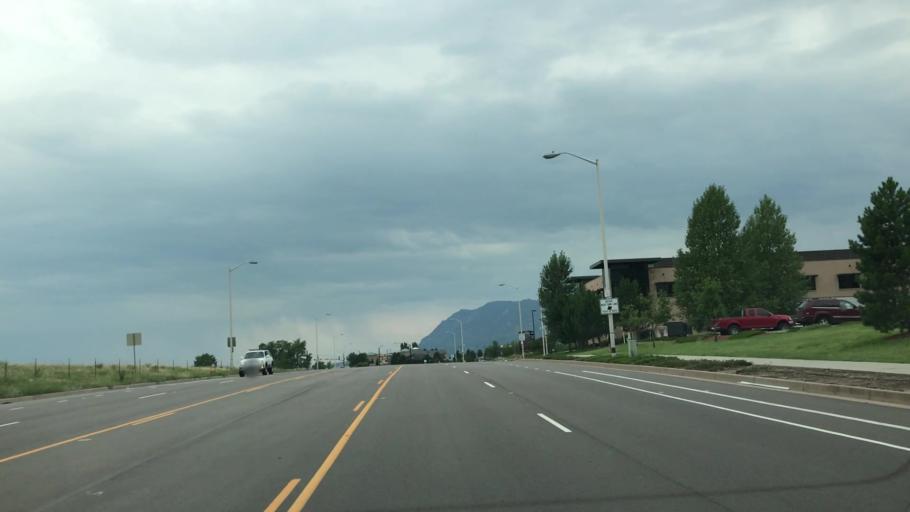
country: US
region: Colorado
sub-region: El Paso County
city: Colorado Springs
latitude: 38.8818
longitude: -104.8477
